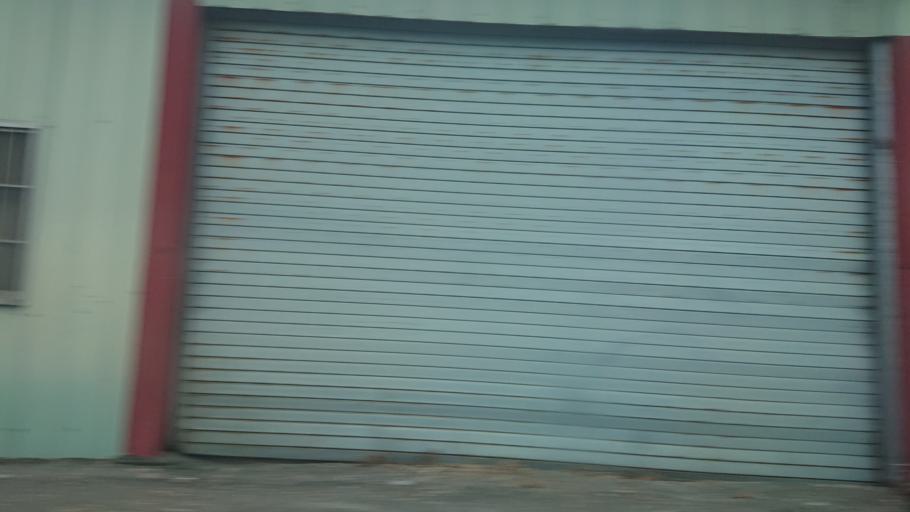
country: TW
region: Taiwan
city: Lugu
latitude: 23.6040
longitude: 120.7081
